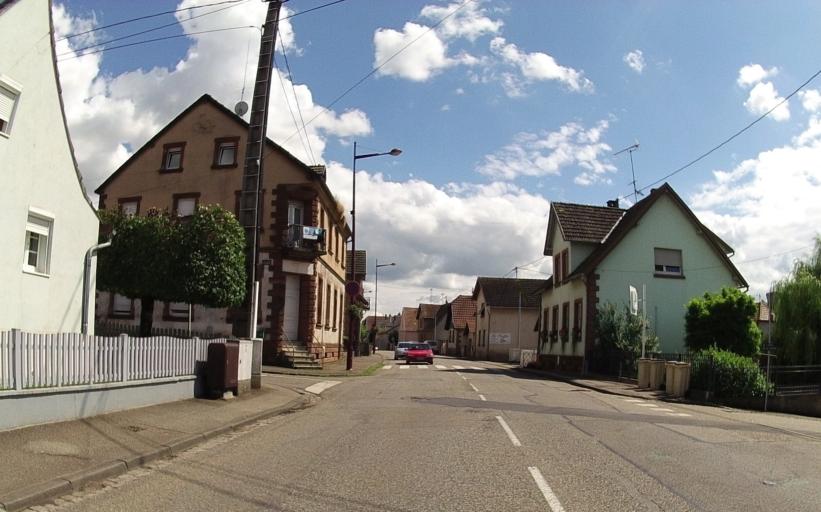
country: FR
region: Alsace
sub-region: Departement du Bas-Rhin
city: Gundershoffen
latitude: 48.9092
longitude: 7.6574
